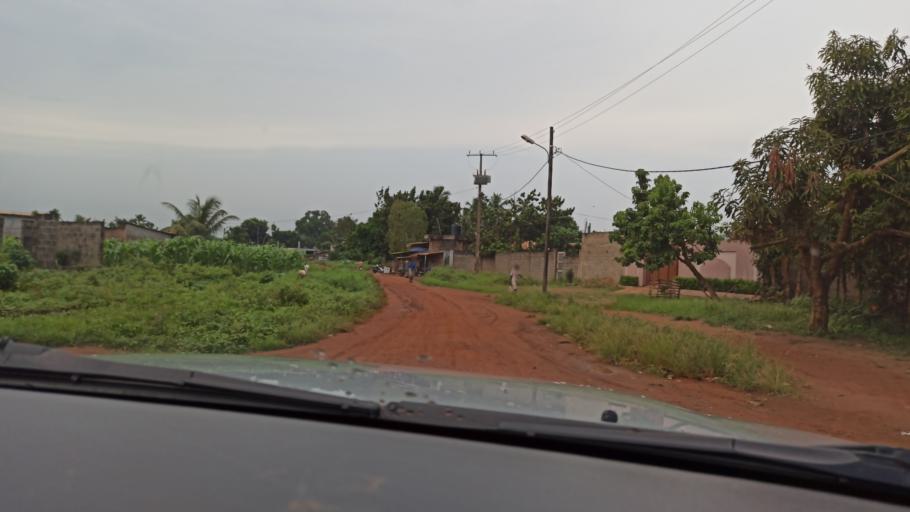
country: BJ
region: Queme
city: Porto-Novo
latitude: 6.4788
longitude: 2.6741
